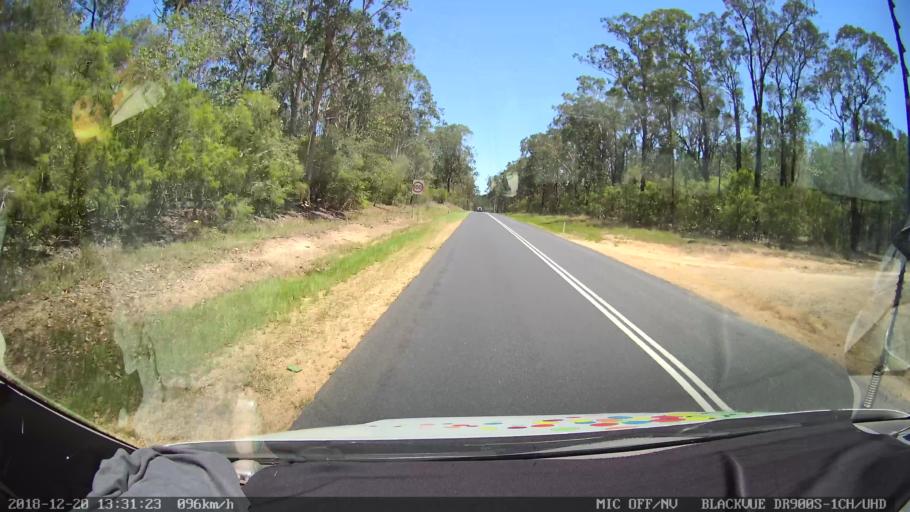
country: AU
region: New South Wales
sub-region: Clarence Valley
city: Gordon
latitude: -29.2172
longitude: 152.9892
